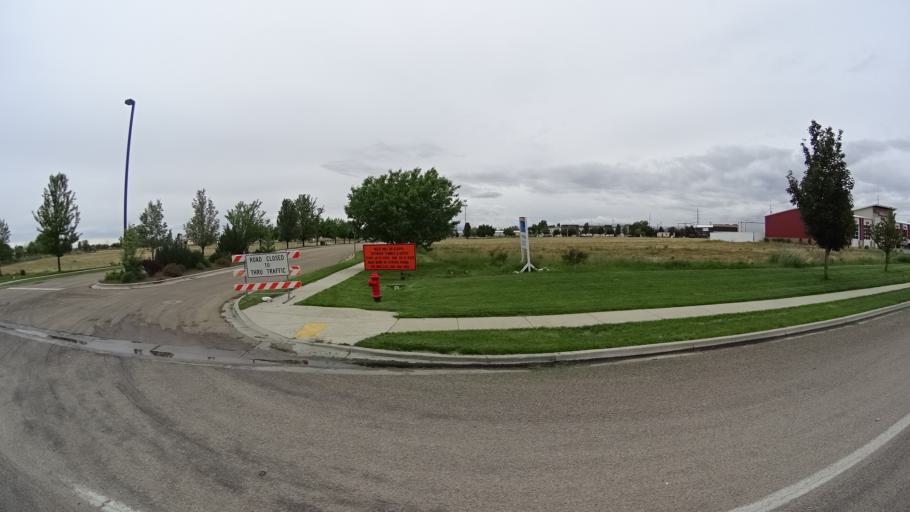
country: US
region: Idaho
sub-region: Ada County
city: Meridian
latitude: 43.6340
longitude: -116.4364
